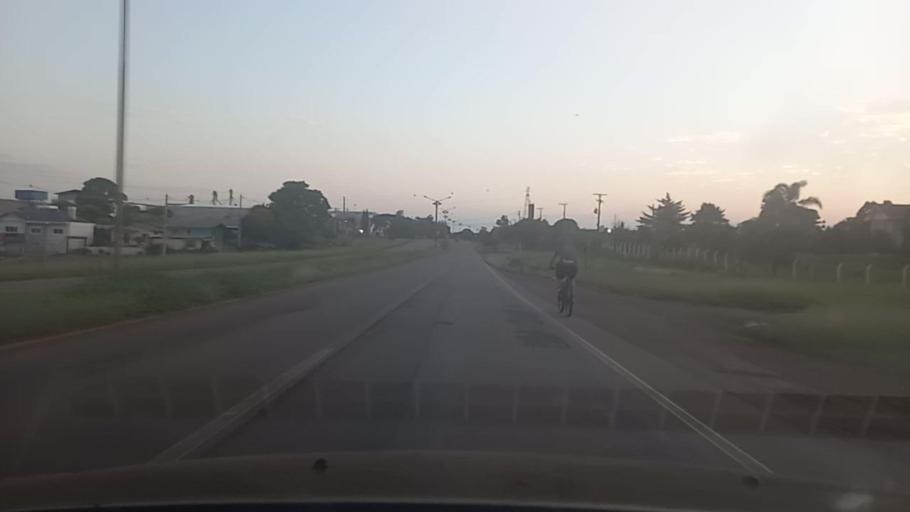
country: BR
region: Rio Grande do Sul
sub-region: Passo Fundo
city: Passo Fundo
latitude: -28.2777
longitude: -52.4498
